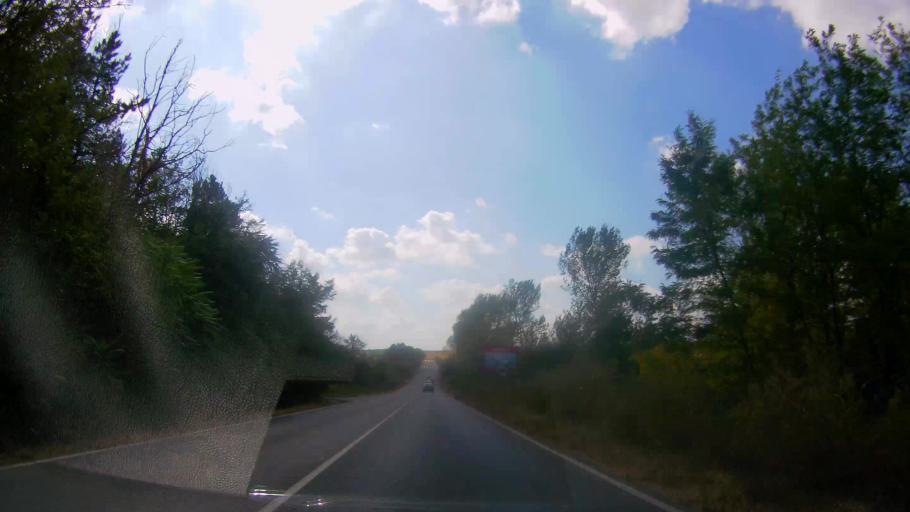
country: BG
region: Ruse
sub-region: Obshtina Ivanovo
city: Ivanovo
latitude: 43.7400
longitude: 25.9115
